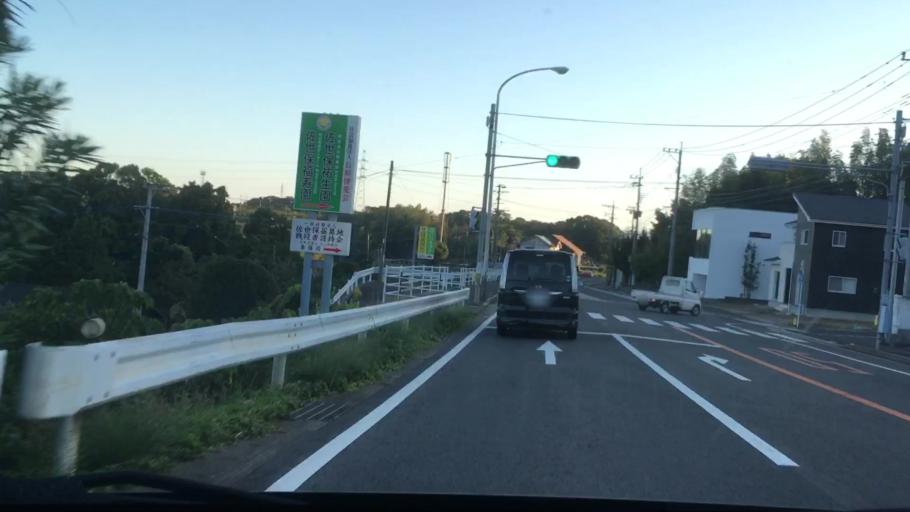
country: JP
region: Nagasaki
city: Sasebo
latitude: 33.0813
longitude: 129.7560
